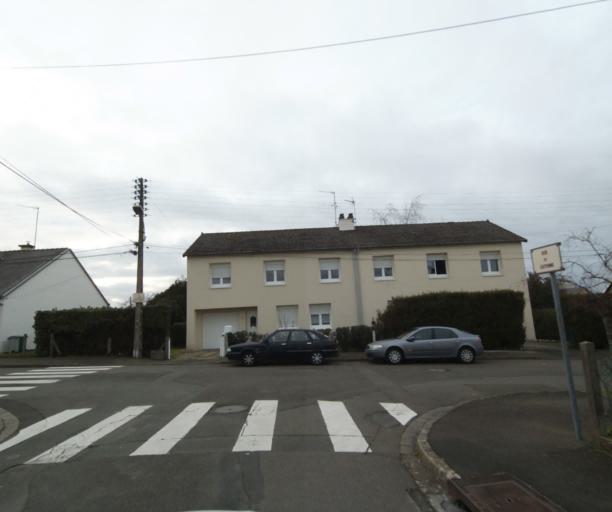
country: FR
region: Pays de la Loire
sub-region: Departement de la Sarthe
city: Le Mans
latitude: 47.9718
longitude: 0.2030
